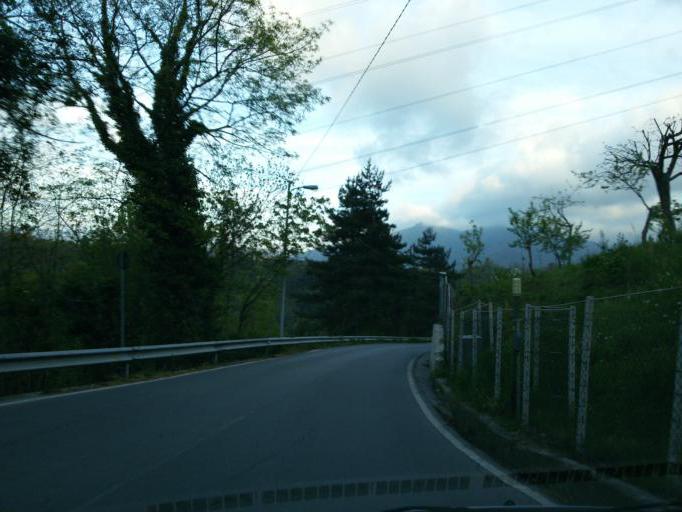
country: IT
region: Liguria
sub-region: Provincia di Genova
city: Santa Marta
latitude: 44.4809
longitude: 8.8851
